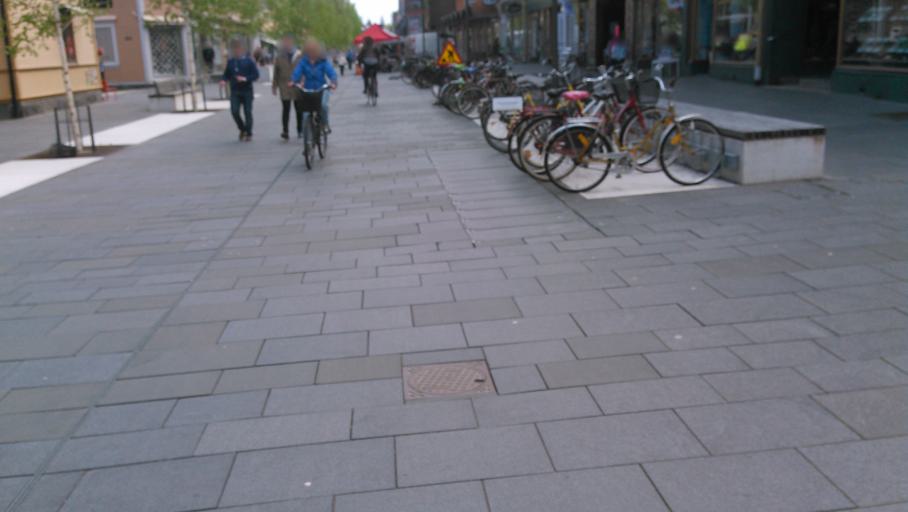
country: SE
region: Vaesterbotten
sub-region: Umea Kommun
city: Umea
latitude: 63.8268
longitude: 20.2574
